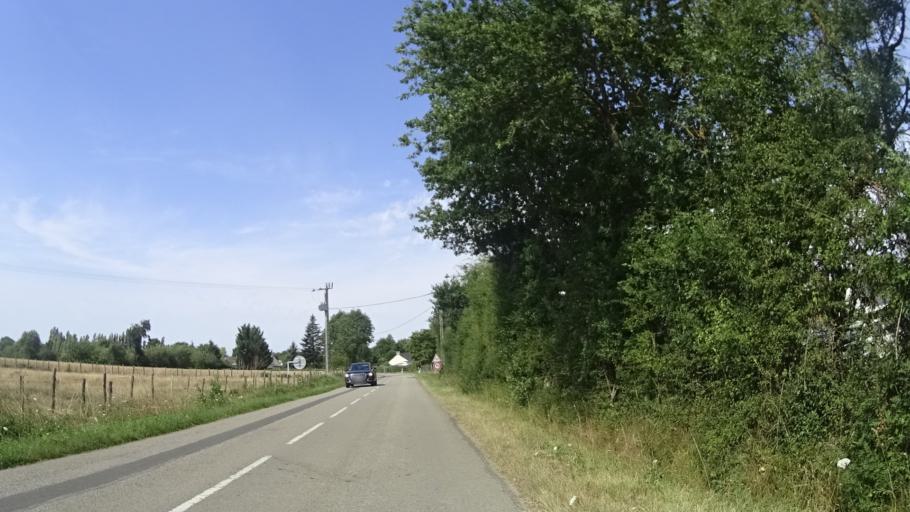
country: FR
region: Pays de la Loire
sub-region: Departement de la Loire-Atlantique
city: Saffre
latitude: 47.4890
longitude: -1.6068
